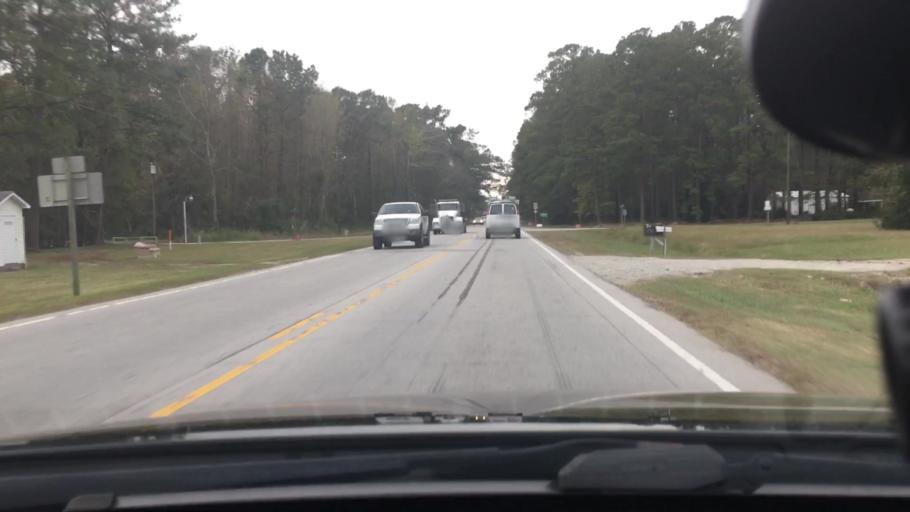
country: US
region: North Carolina
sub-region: Craven County
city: Vanceboro
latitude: 35.2619
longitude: -77.1022
